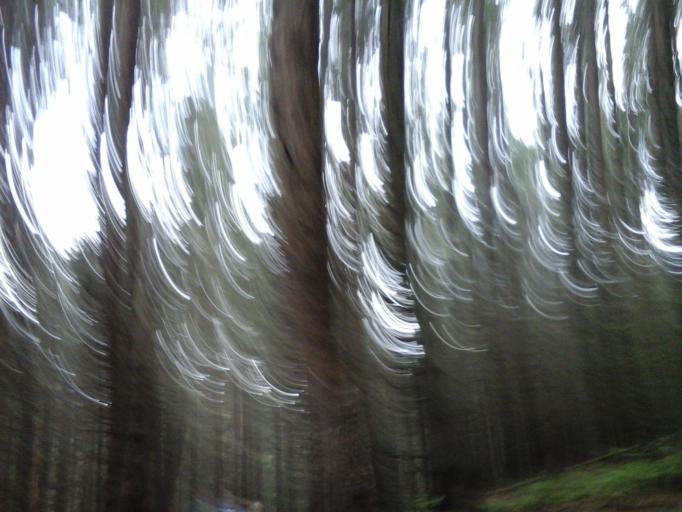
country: PL
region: Lesser Poland Voivodeship
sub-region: Powiat tatrzanski
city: Zakopane
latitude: 49.2644
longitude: 19.9917
